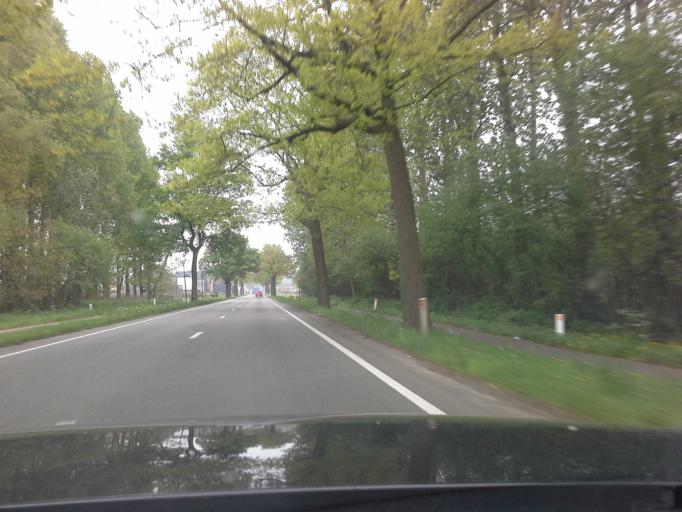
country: BE
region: Flanders
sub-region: Provincie Antwerpen
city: Kasterlee
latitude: 51.2106
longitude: 4.9775
